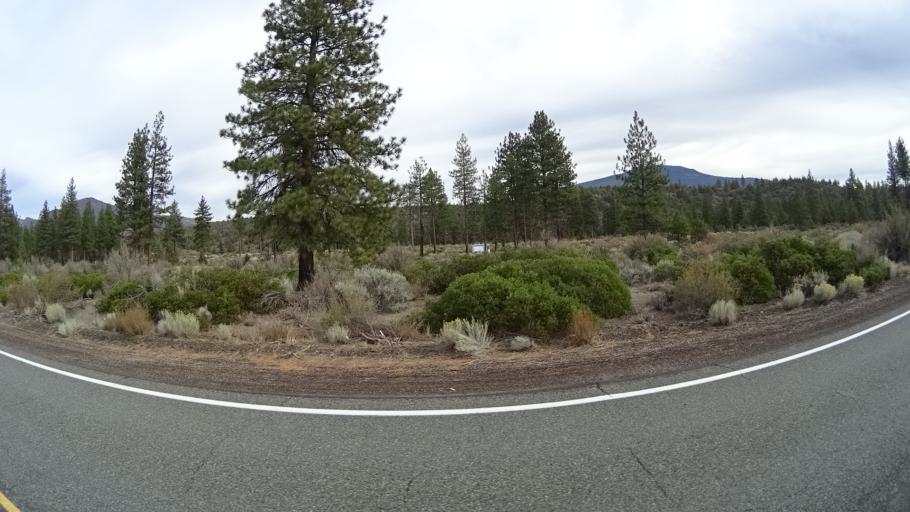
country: US
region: California
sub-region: Siskiyou County
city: Weed
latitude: 41.5422
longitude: -122.2459
